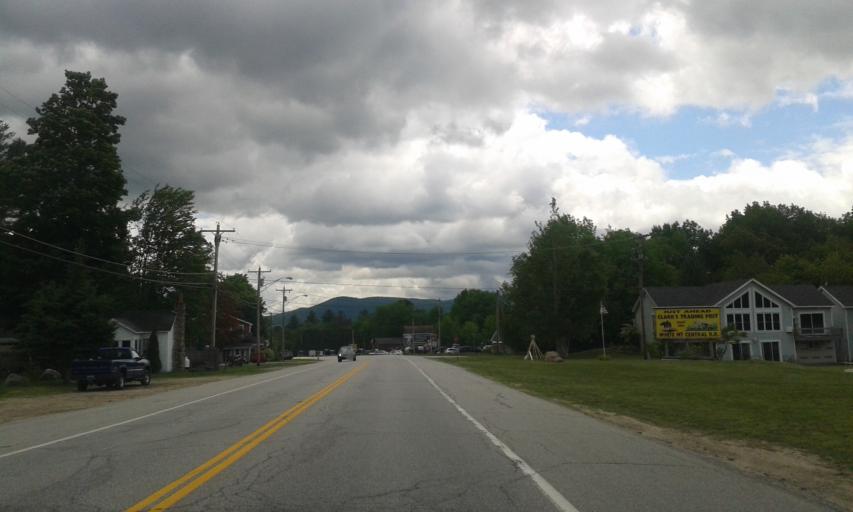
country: US
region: New Hampshire
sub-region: Grafton County
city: Woodstock
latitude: 44.0717
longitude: -71.6853
